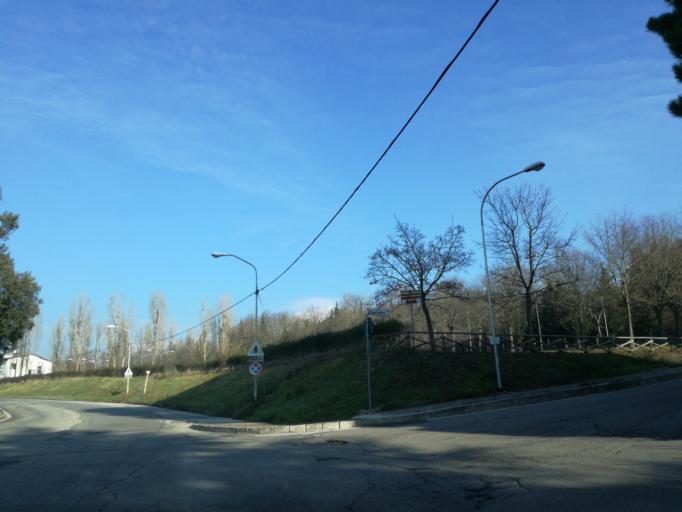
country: IT
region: Umbria
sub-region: Provincia di Perugia
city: Perugia
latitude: 43.1099
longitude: 12.3662
